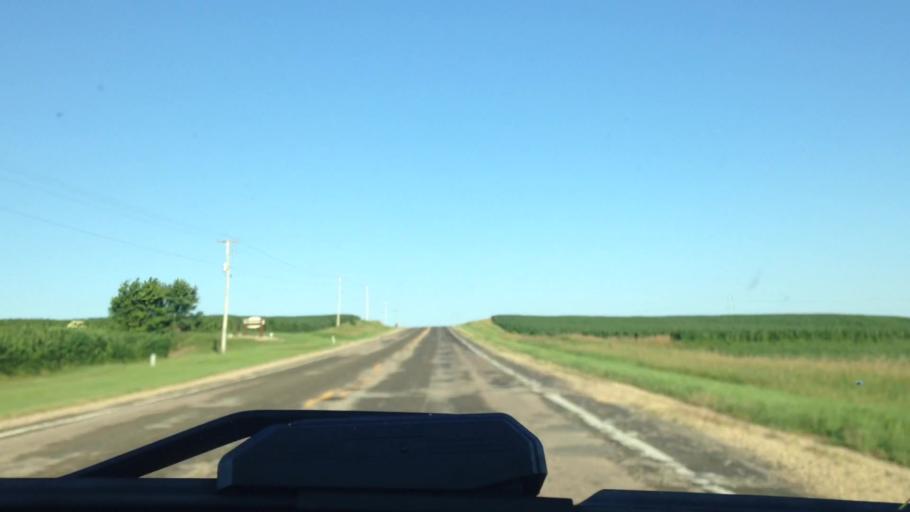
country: US
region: Wisconsin
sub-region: Columbia County
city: Poynette
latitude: 43.3377
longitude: -89.3915
